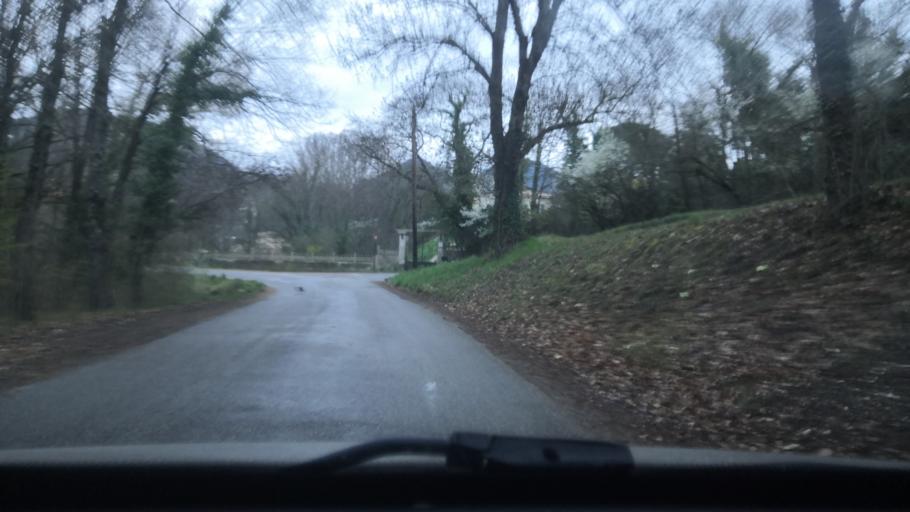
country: FR
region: Rhone-Alpes
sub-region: Departement de la Drome
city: Dieulefit
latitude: 44.5200
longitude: 5.0624
